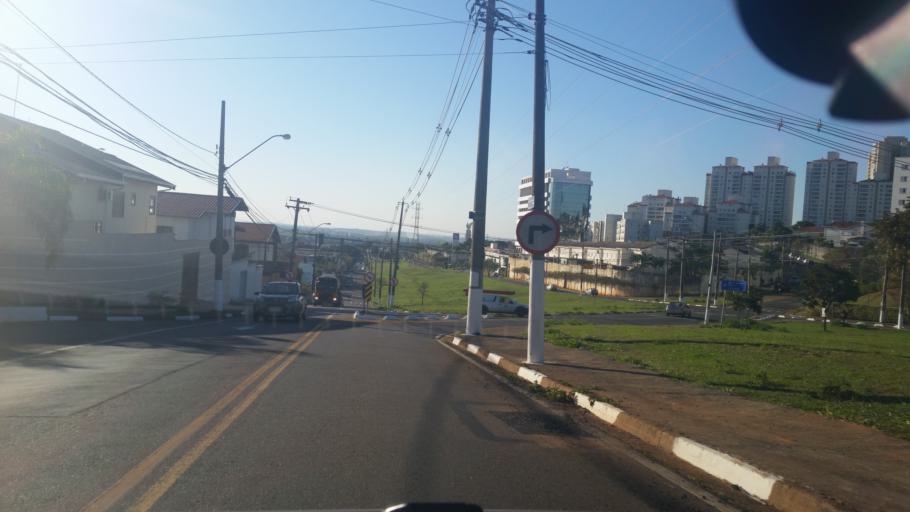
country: BR
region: Sao Paulo
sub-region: Campinas
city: Campinas
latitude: -22.8594
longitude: -47.0541
